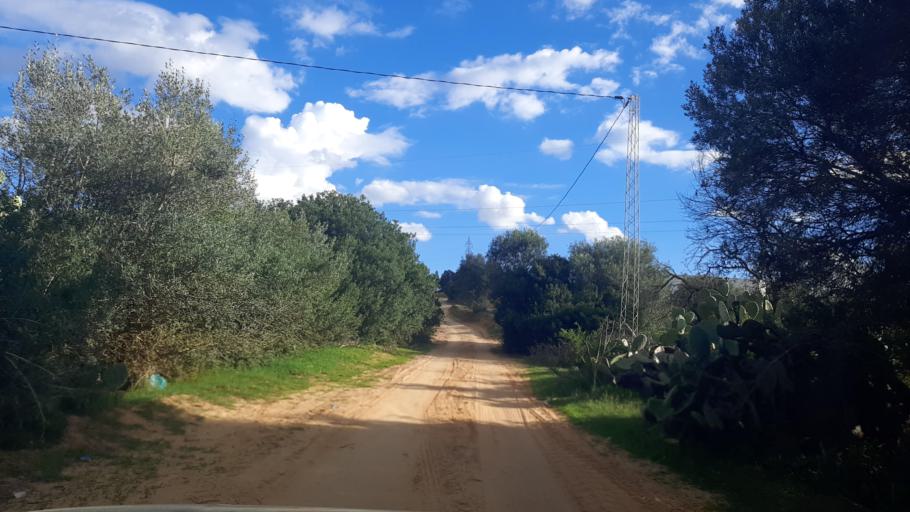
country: TN
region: Nabul
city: Bu `Urqub
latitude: 36.4400
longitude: 10.5082
